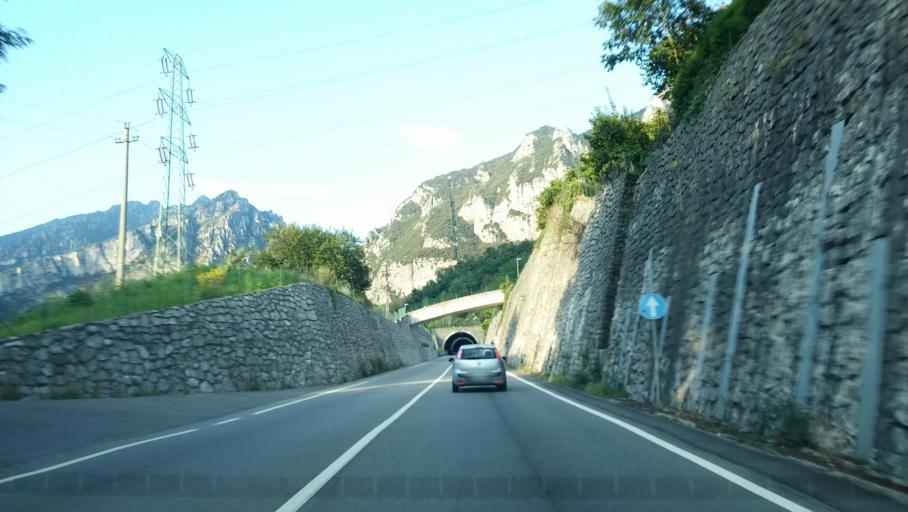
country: IT
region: Lombardy
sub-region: Provincia di Lecco
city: Lecco
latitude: 45.8631
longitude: 9.4162
